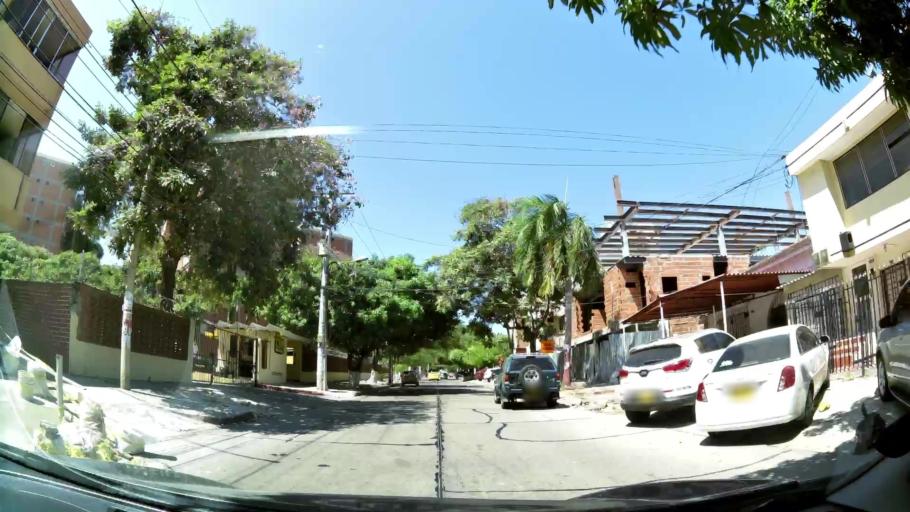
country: CO
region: Atlantico
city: Barranquilla
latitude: 10.9916
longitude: -74.8030
